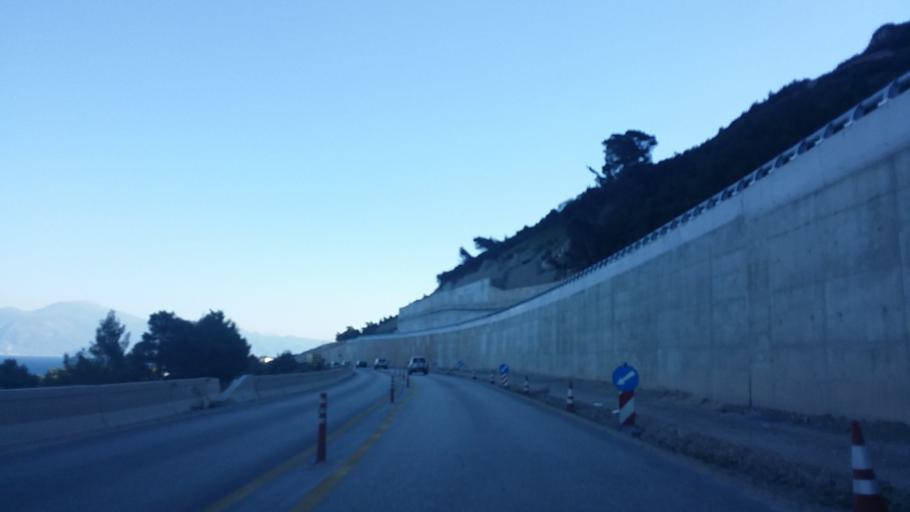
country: GR
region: West Greece
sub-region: Nomos Achaias
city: Ano Kastritsion
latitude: 38.3230
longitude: 21.9055
